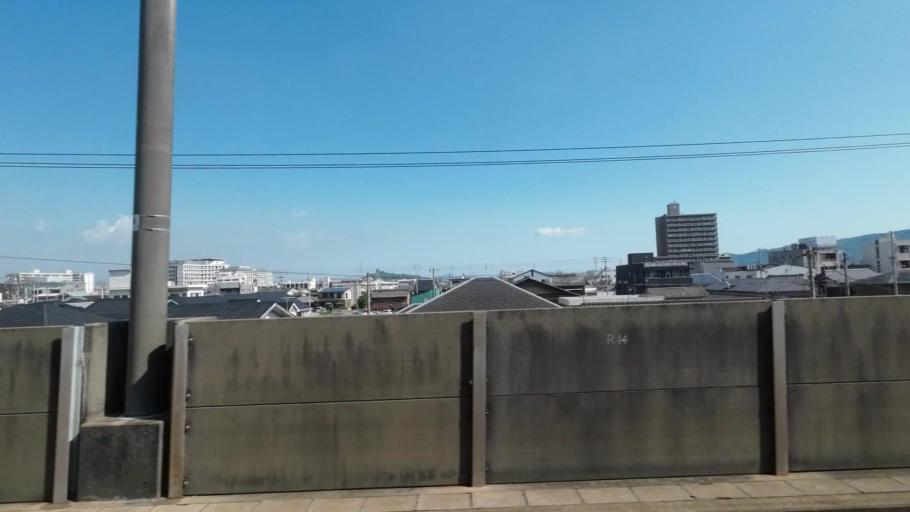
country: JP
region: Kagawa
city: Sakaidecho
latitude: 34.3139
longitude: 133.8644
